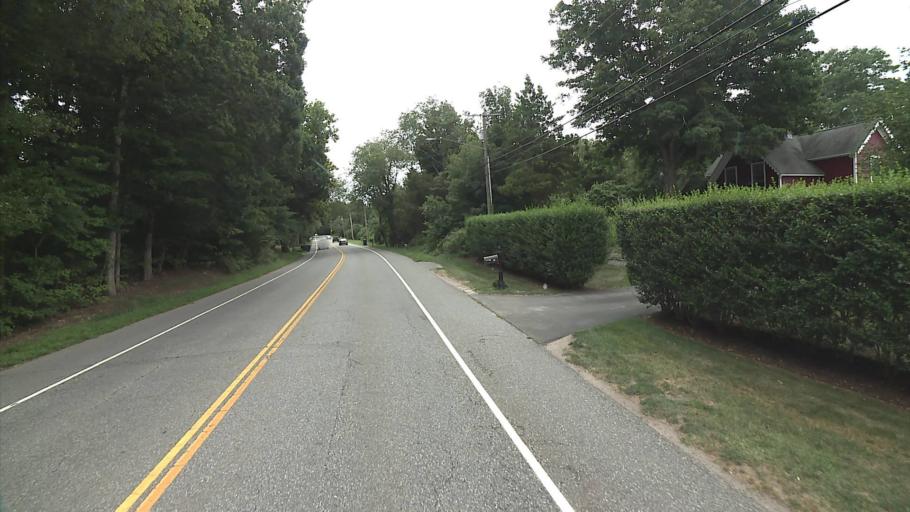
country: US
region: Connecticut
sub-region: Middlesex County
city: Old Saybrook Center
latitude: 41.3005
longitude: -72.3262
